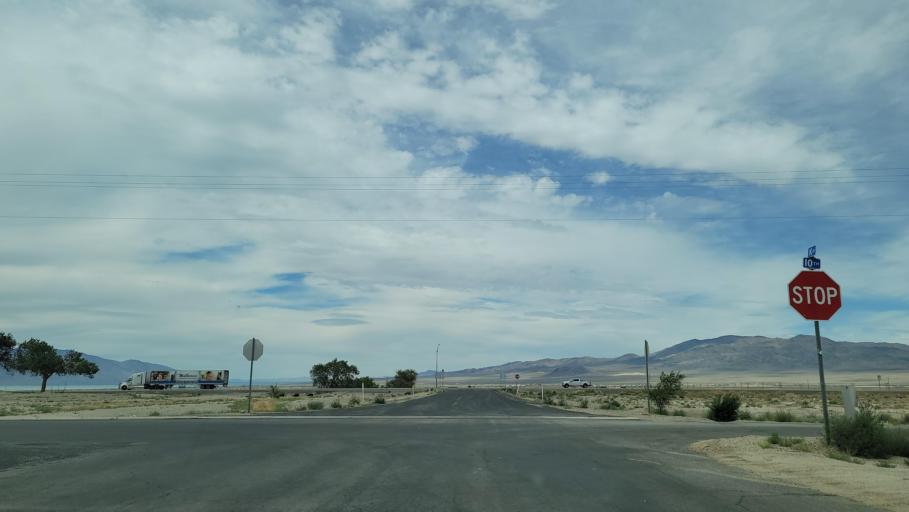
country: US
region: Nevada
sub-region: Mineral County
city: Hawthorne
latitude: 38.5321
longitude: -118.6190
